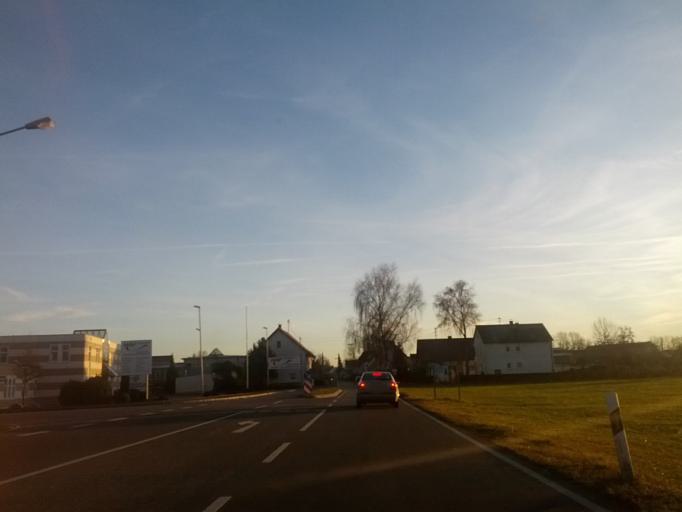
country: DE
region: Bavaria
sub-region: Swabia
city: Fellheim
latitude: 48.0783
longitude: 10.1505
